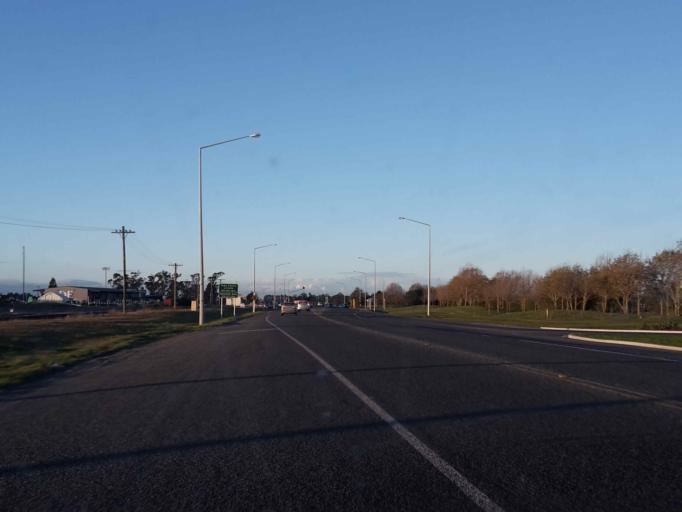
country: NZ
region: Canterbury
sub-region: Selwyn District
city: Rolleston
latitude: -43.5901
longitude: 172.3804
